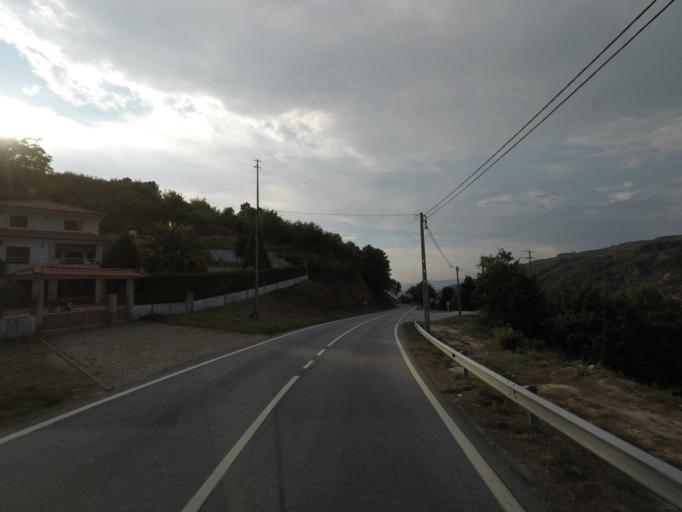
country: PT
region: Porto
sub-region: Baiao
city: Valadares
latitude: 41.2157
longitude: -7.9813
